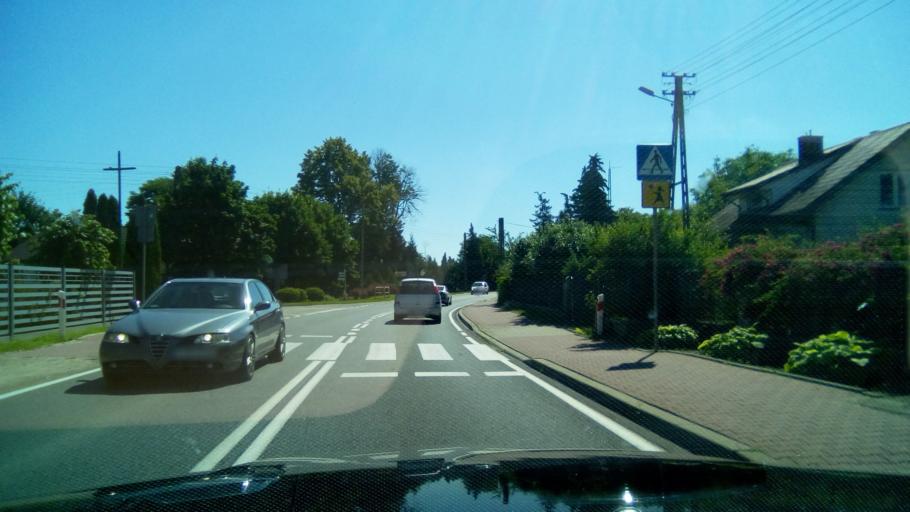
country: PL
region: Lodz Voivodeship
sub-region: Powiat tomaszowski
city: Inowlodz
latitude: 51.5262
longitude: 20.2204
